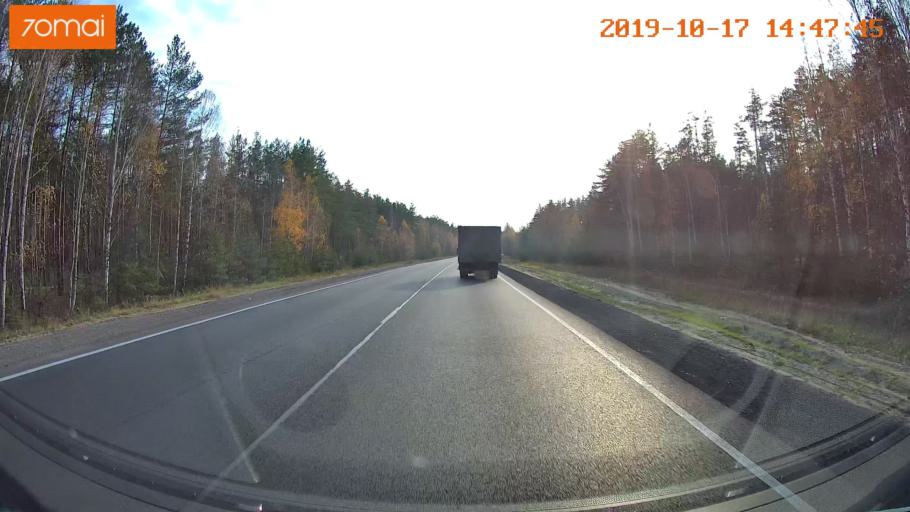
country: RU
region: Rjazan
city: Solotcha
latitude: 54.7671
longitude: 39.8577
